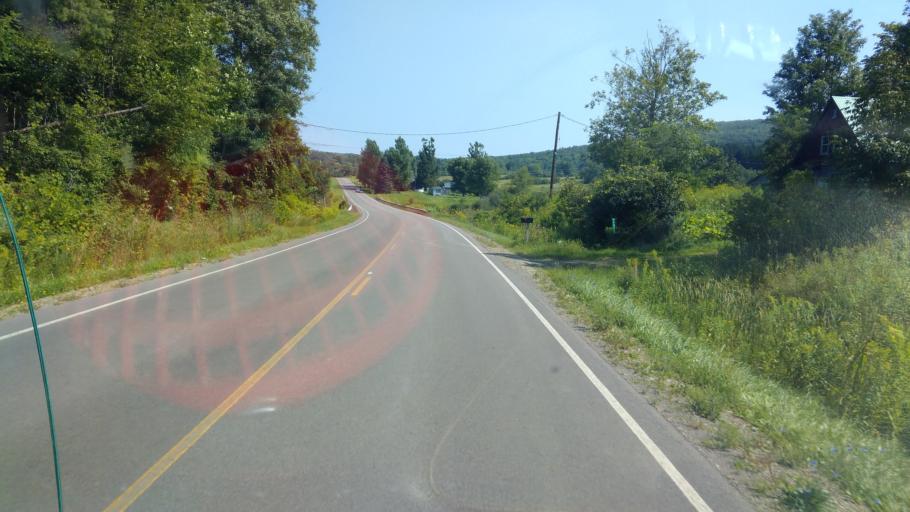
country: US
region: New York
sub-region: Allegany County
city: Belmont
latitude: 42.2793
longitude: -78.0339
